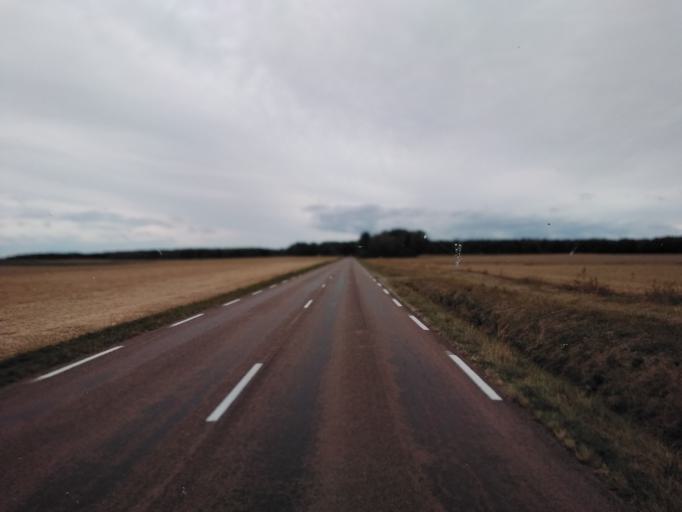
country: FR
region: Champagne-Ardenne
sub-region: Departement de l'Aube
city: Vendeuvre-sur-Barse
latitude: 48.2239
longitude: 4.4520
